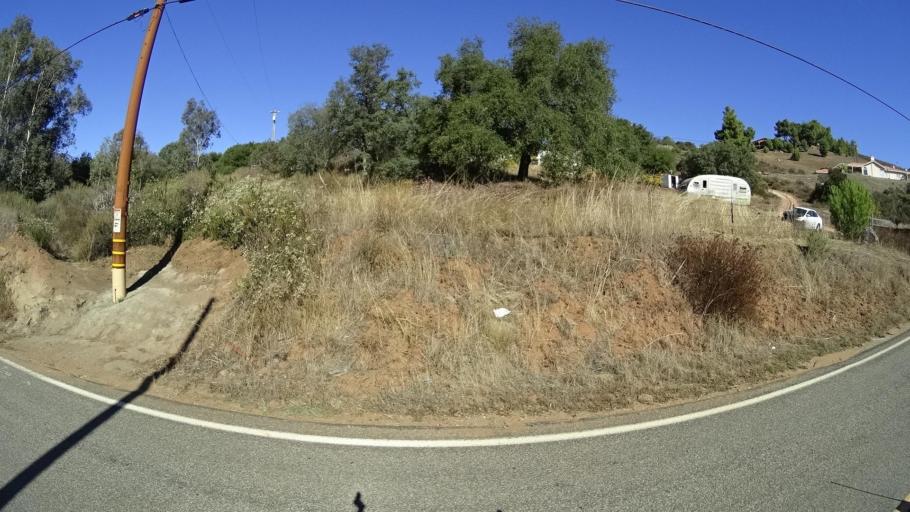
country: US
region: California
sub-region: San Diego County
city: Jamul
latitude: 32.6855
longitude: -116.7521
